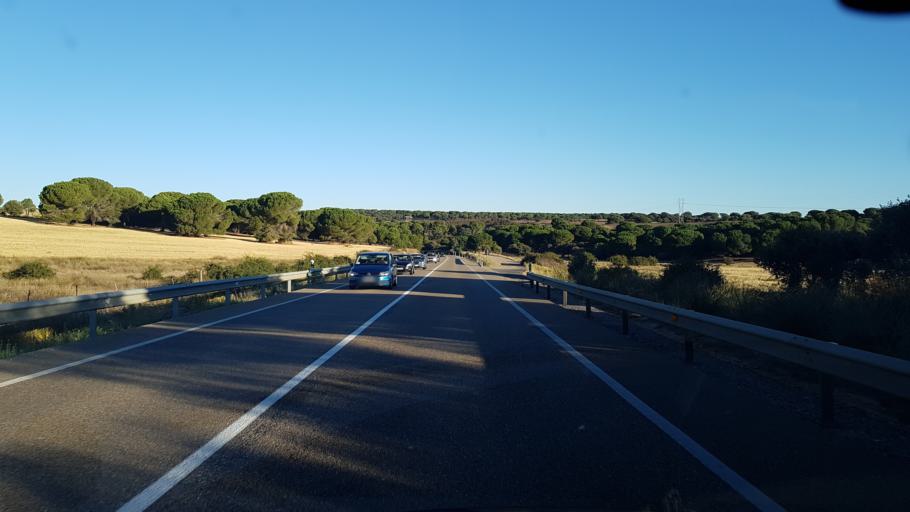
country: ES
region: Castille and Leon
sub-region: Provincia de Zamora
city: Roales
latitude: 41.5313
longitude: -5.8224
